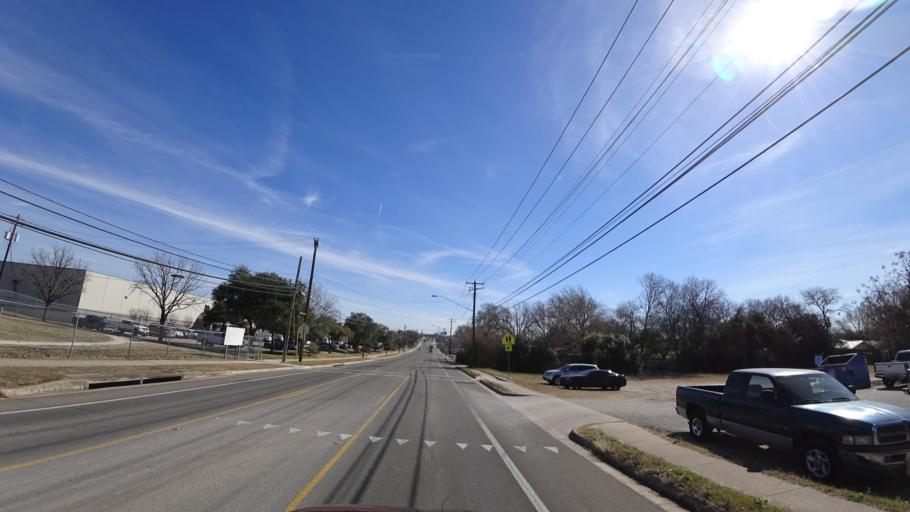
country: US
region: Texas
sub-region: Travis County
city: Wells Branch
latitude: 30.3820
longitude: -97.6929
